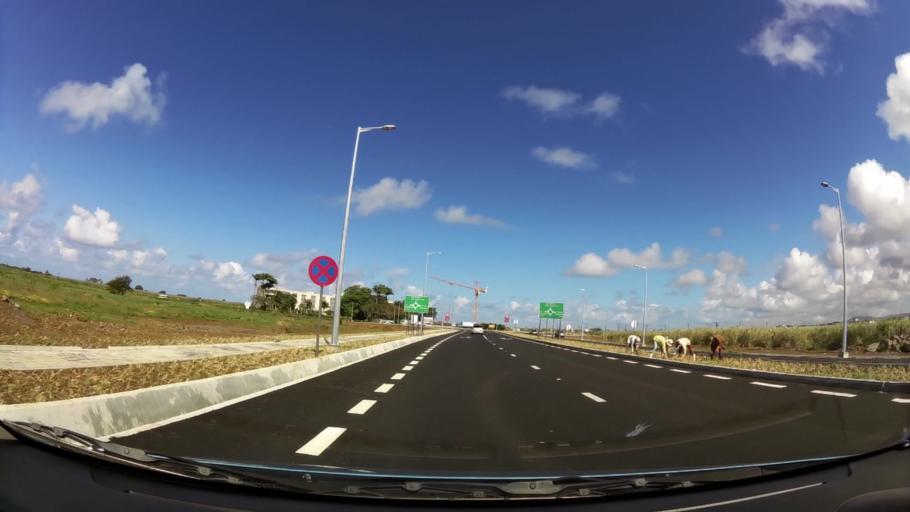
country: MU
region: Grand Port
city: Plaine Magnien
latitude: -20.4377
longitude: 57.6721
